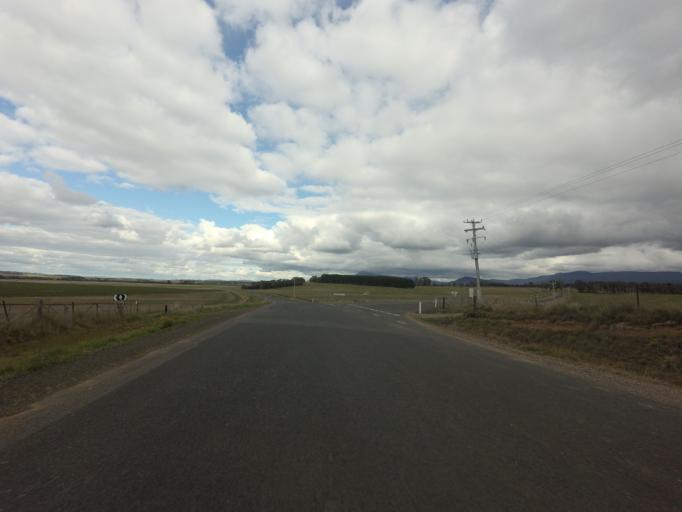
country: AU
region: Tasmania
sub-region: Northern Midlands
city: Longford
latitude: -41.7733
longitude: 147.0904
